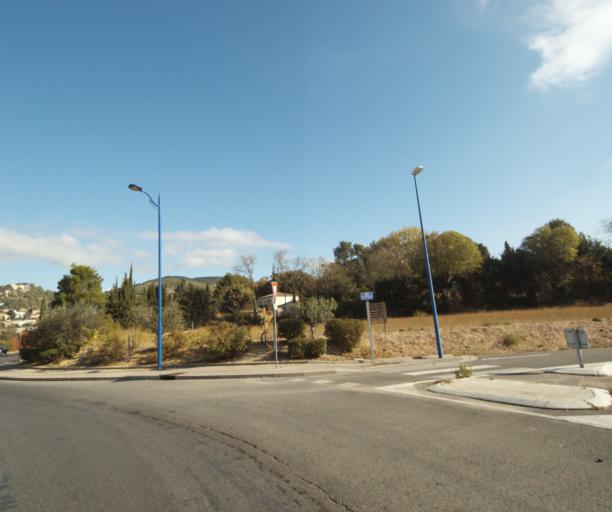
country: FR
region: Provence-Alpes-Cote d'Azur
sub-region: Departement des Bouches-du-Rhone
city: Allauch
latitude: 43.3271
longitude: 5.4826
